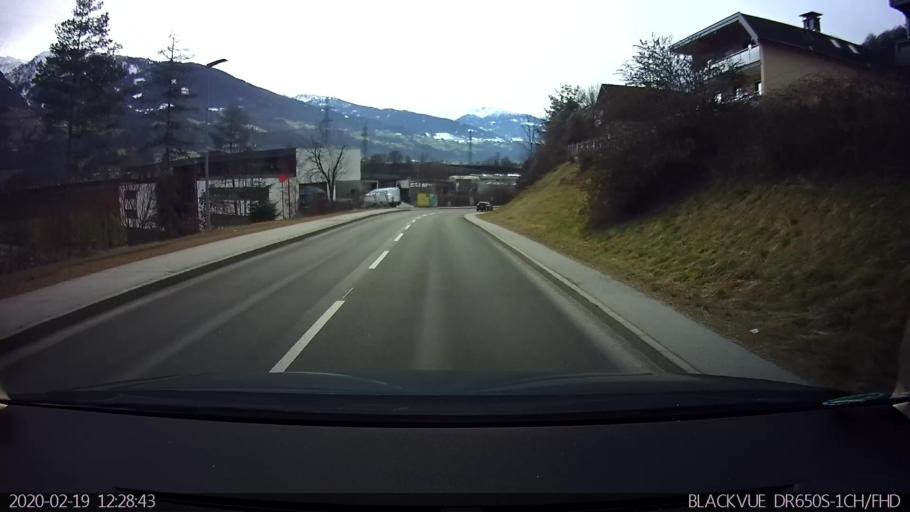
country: AT
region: Tyrol
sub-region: Politischer Bezirk Schwaz
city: Stans
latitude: 47.3657
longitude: 11.7128
